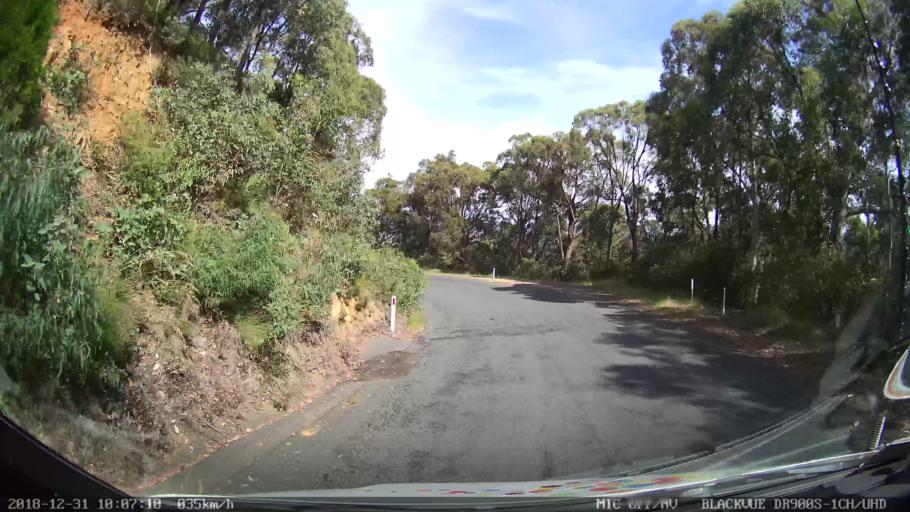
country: AU
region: New South Wales
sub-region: Snowy River
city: Jindabyne
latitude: -36.5313
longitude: 148.1854
